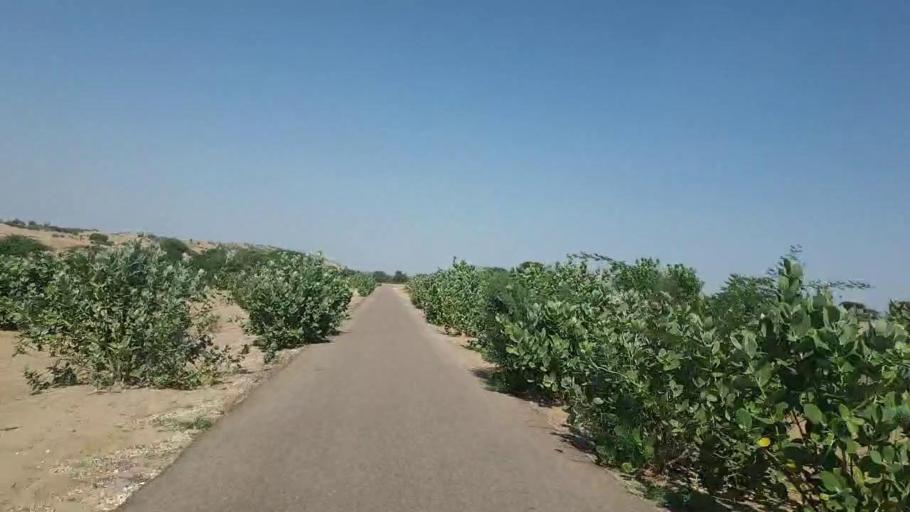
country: PK
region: Sindh
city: Chor
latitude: 25.6068
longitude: 70.3137
